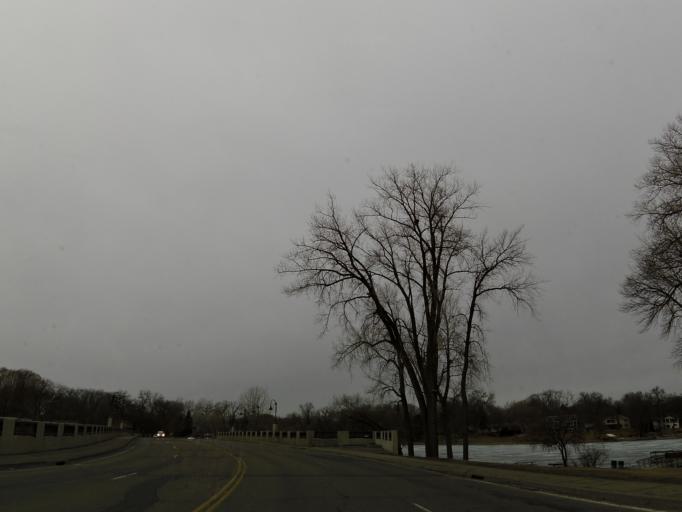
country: US
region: Minnesota
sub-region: Scott County
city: Prior Lake
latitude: 44.7187
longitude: -93.4347
